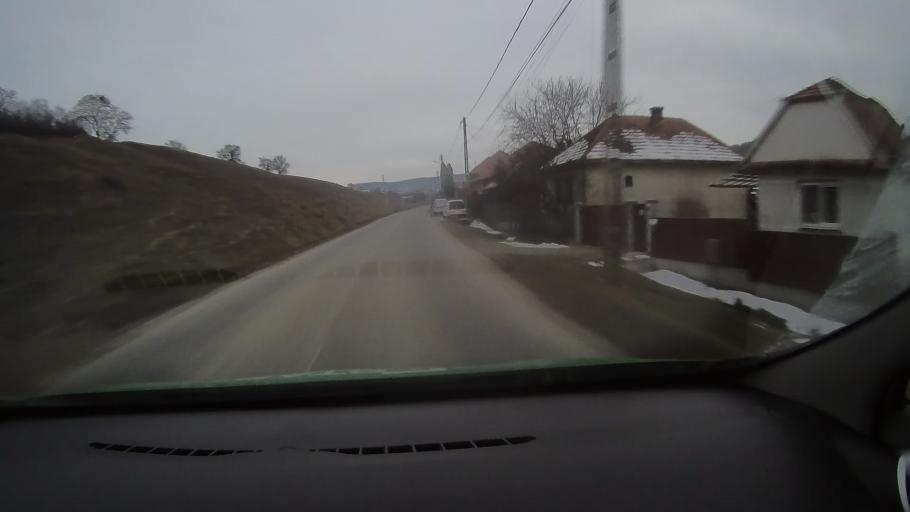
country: RO
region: Harghita
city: Taureni
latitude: 46.2562
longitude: 25.2529
